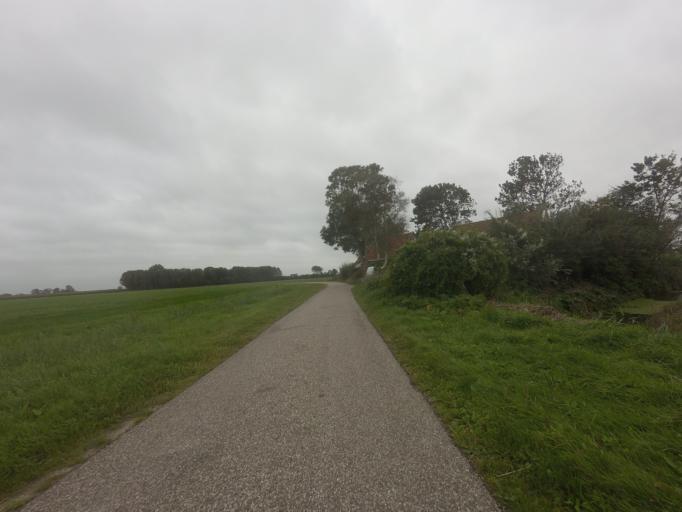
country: NL
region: Friesland
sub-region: Gemeente Ferwerderadiel
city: Ferwert
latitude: 53.3400
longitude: 5.8566
